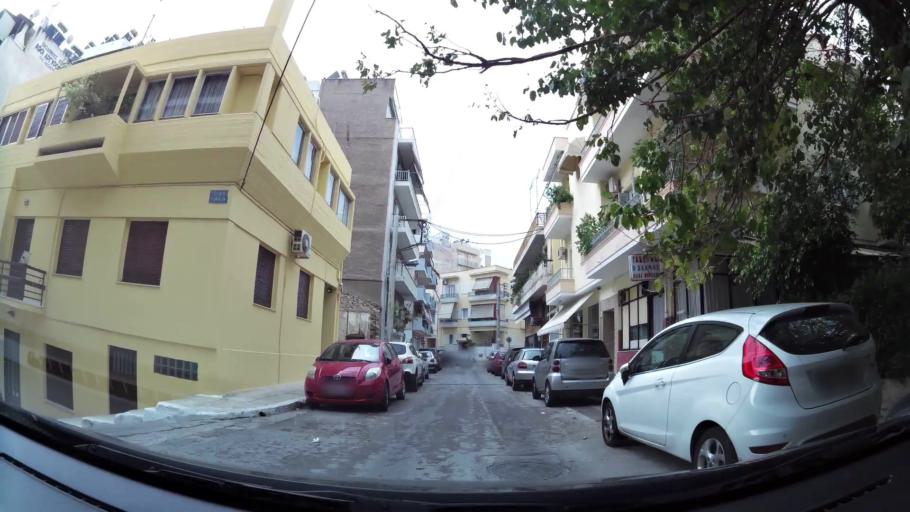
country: GR
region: Attica
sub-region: Nomos Attikis
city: Piraeus
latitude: 37.9448
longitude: 23.6570
